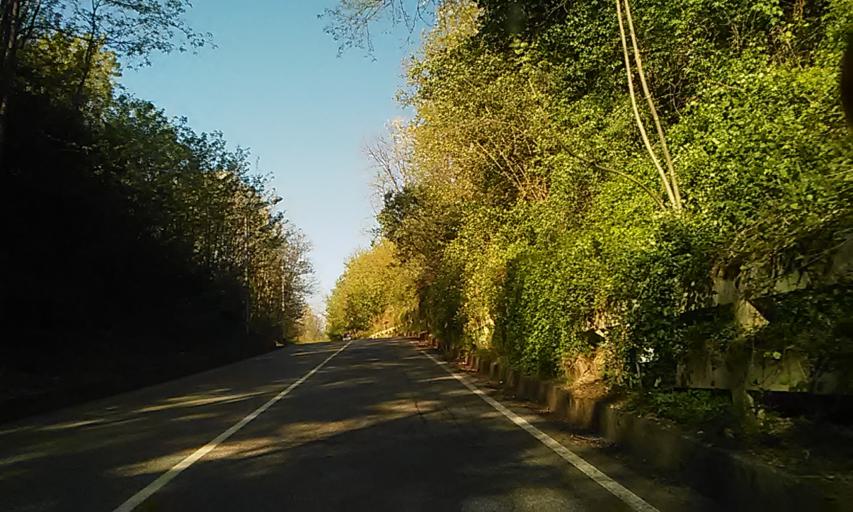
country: IT
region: Piedmont
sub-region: Provincia di Novara
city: Ghemme
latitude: 45.6078
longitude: 8.4226
